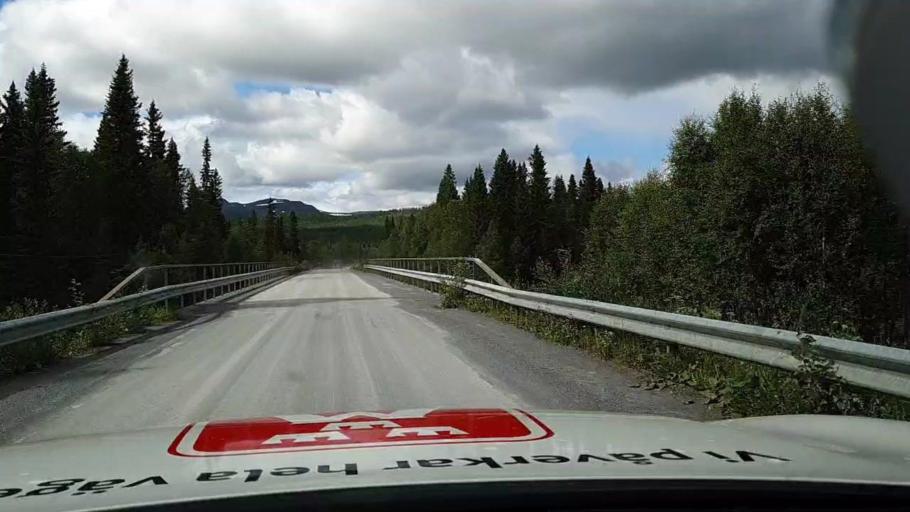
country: SE
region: Jaemtland
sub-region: Krokoms Kommun
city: Valla
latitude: 63.7021
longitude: 13.5978
